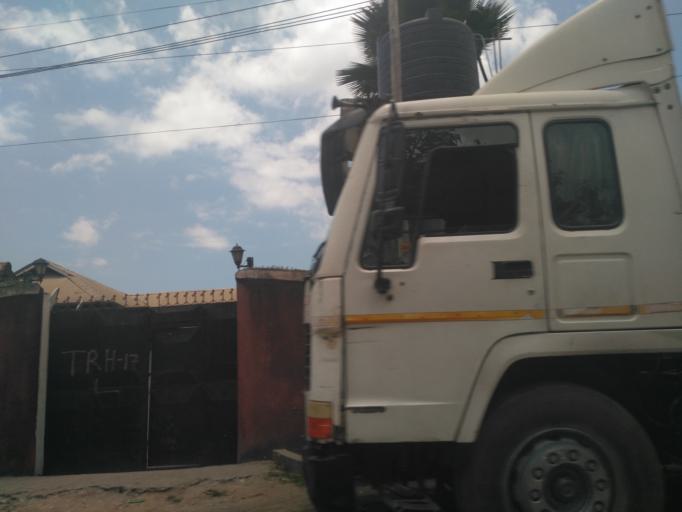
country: TZ
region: Dar es Salaam
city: Dar es Salaam
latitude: -6.8643
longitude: 39.2826
